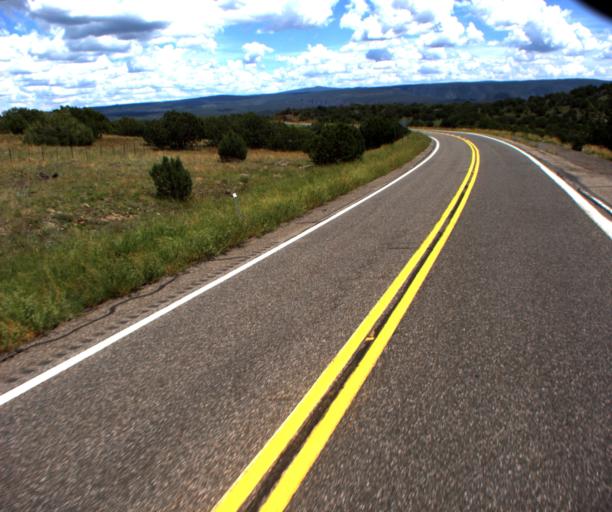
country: US
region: Arizona
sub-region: Gila County
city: Pine
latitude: 34.4865
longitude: -111.6220
